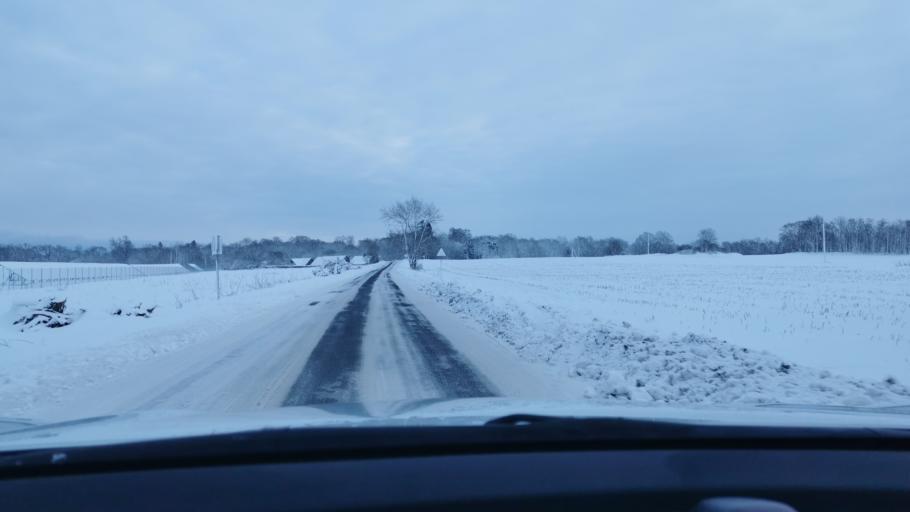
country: EE
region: Laeaene-Virumaa
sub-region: Viru-Nigula vald
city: Kunda
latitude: 59.4833
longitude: 26.5164
